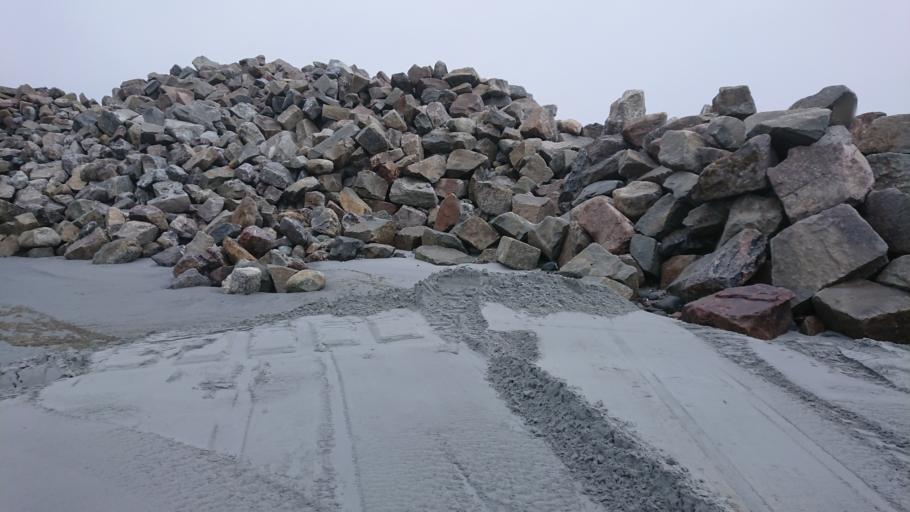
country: DK
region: North Denmark
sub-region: Frederikshavn Kommune
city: Skagen
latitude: 57.7193
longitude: 10.6074
